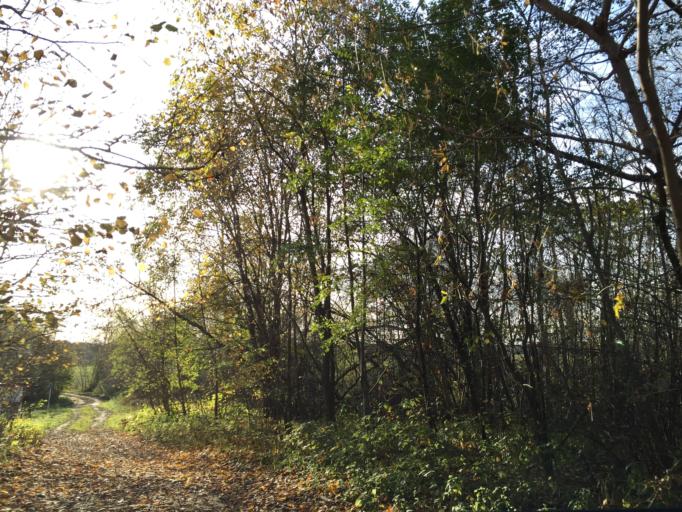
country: LV
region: Skriveri
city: Skriveri
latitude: 56.6243
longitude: 25.1214
